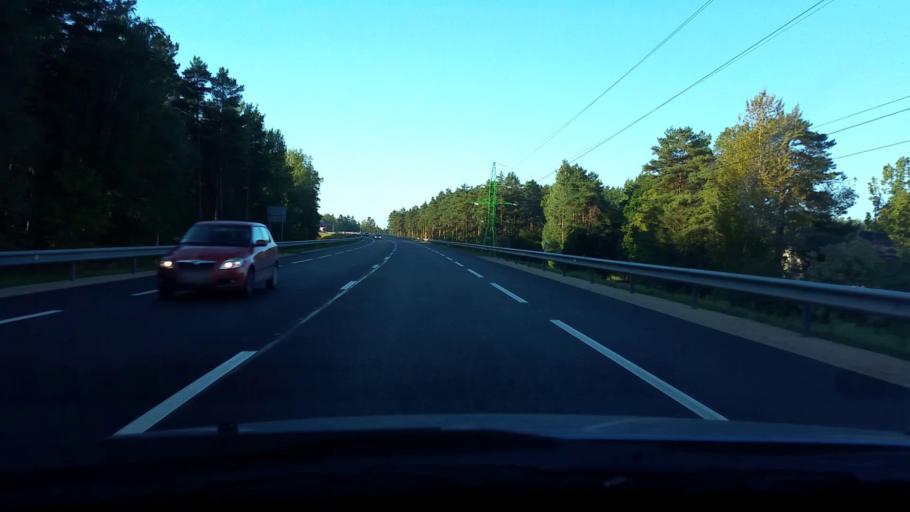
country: LV
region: Riga
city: Bergi
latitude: 57.0143
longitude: 24.3086
